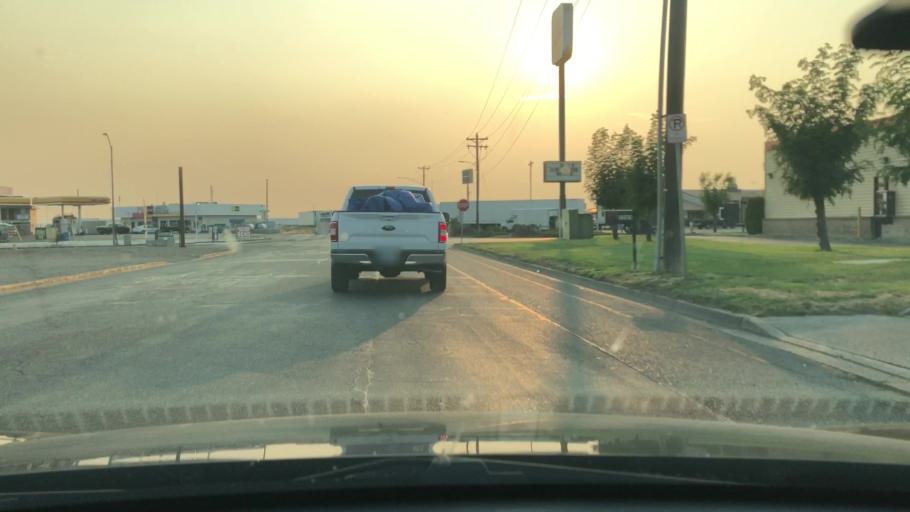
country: US
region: Washington
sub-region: Franklin County
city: Pasco
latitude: 46.2628
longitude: -119.0831
